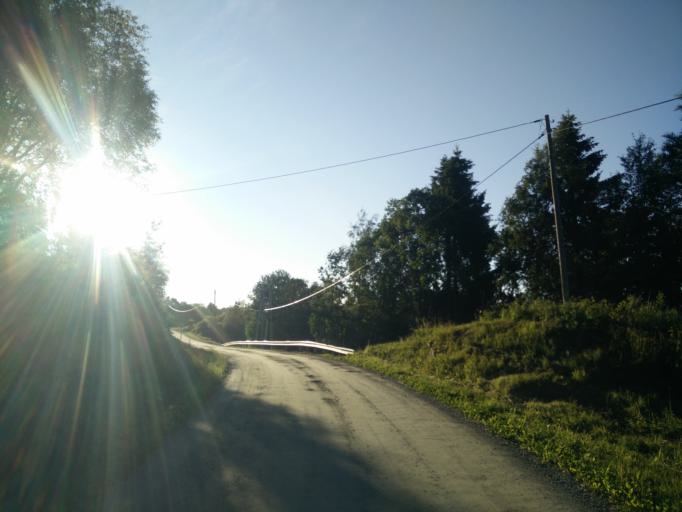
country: NO
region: Sor-Trondelag
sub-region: Skaun
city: Borsa
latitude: 63.3364
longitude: 10.0466
